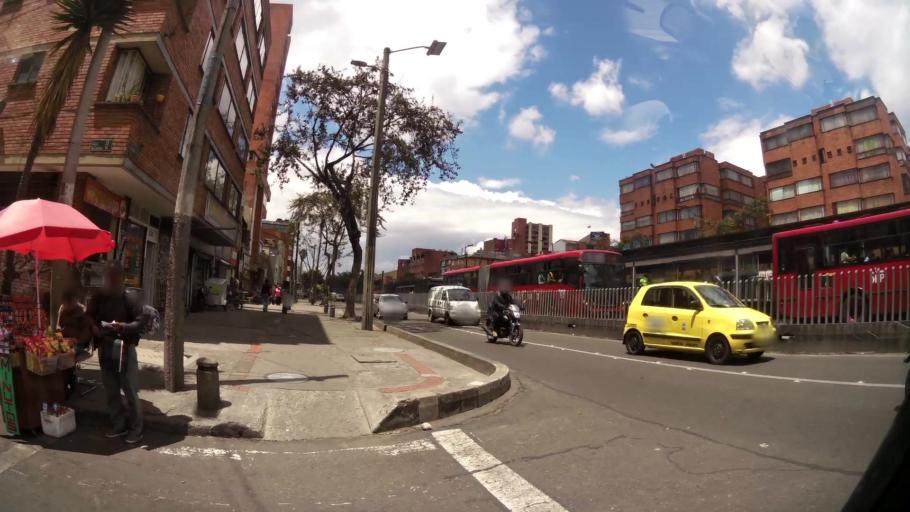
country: CO
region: Bogota D.C.
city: Bogota
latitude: 4.6374
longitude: -74.0670
